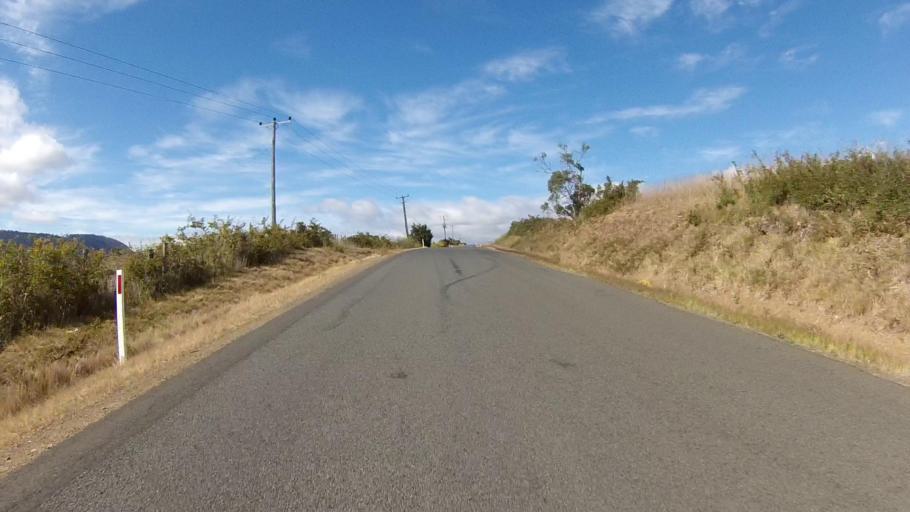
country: AU
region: Tasmania
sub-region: Brighton
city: Old Beach
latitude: -42.7586
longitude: 147.2800
